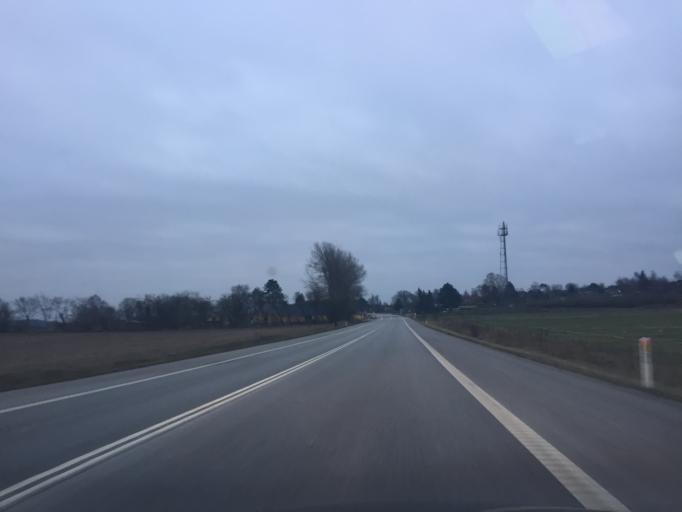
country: DK
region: Capital Region
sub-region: Halsnaes Kommune
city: Frederiksvaerk
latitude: 55.9377
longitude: 12.0480
